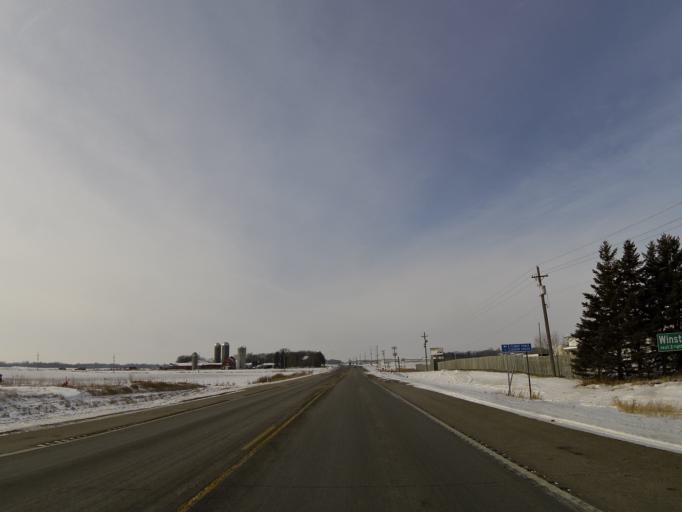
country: US
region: Minnesota
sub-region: McLeod County
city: Lester Prairie
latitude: 44.9063
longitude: -94.0280
